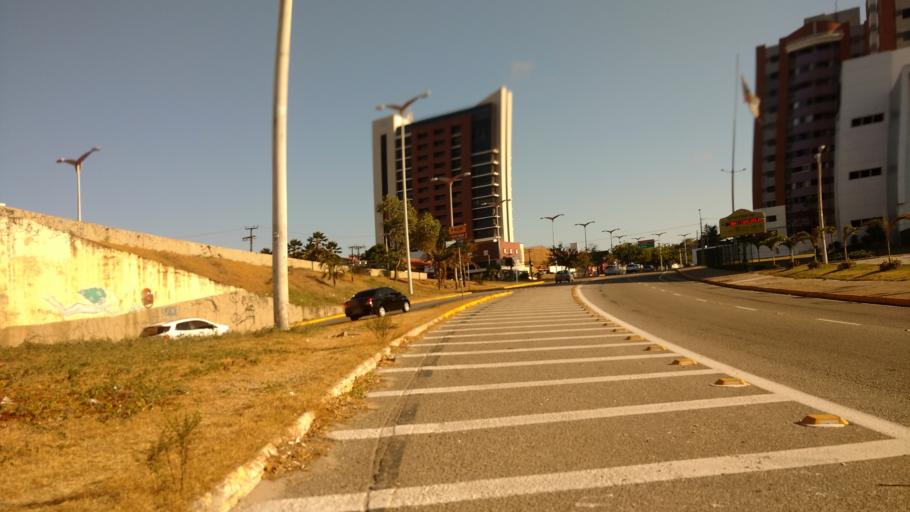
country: BR
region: Ceara
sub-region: Fortaleza
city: Fortaleza
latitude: -3.7595
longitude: -38.4835
